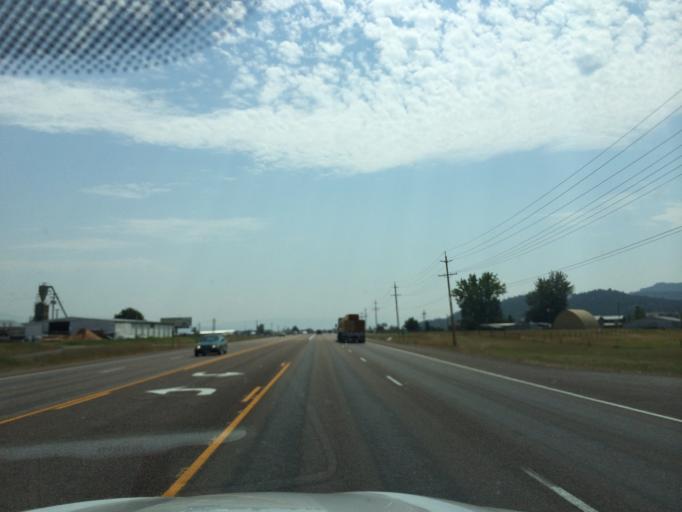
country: US
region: Montana
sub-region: Flathead County
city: Kalispell
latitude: 48.1413
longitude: -114.2813
